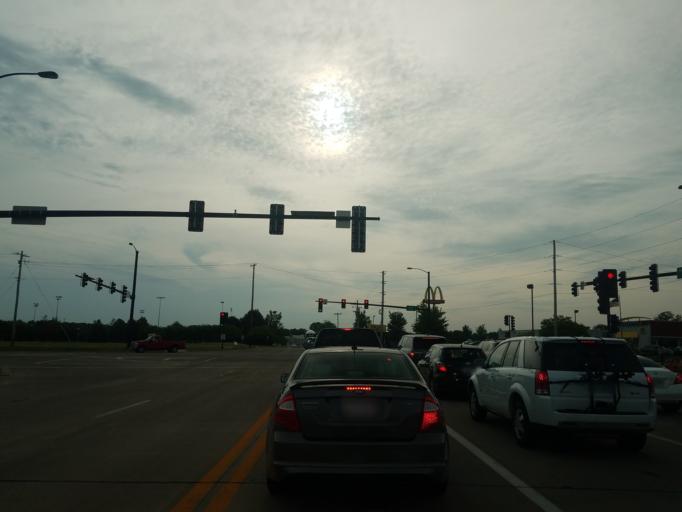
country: US
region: Illinois
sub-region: McLean County
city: Bloomington
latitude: 40.4500
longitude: -88.9928
